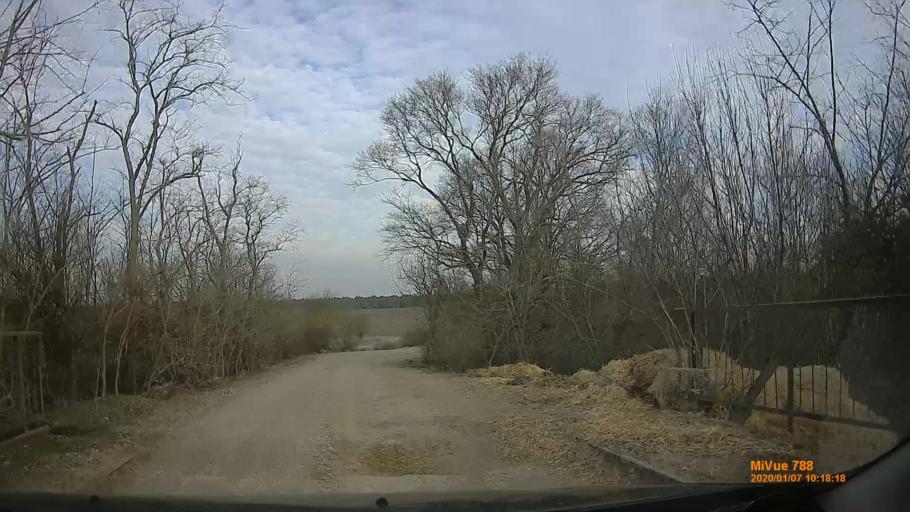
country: HU
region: Gyor-Moson-Sopron
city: Rajka
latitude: 47.9176
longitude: 17.1940
